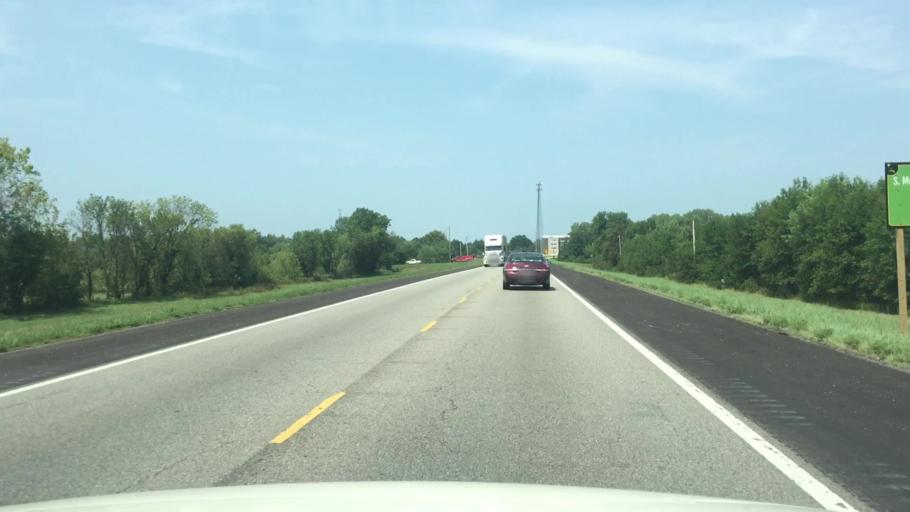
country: US
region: Kansas
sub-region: Crawford County
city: Pittsburg
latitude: 37.3758
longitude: -94.7079
